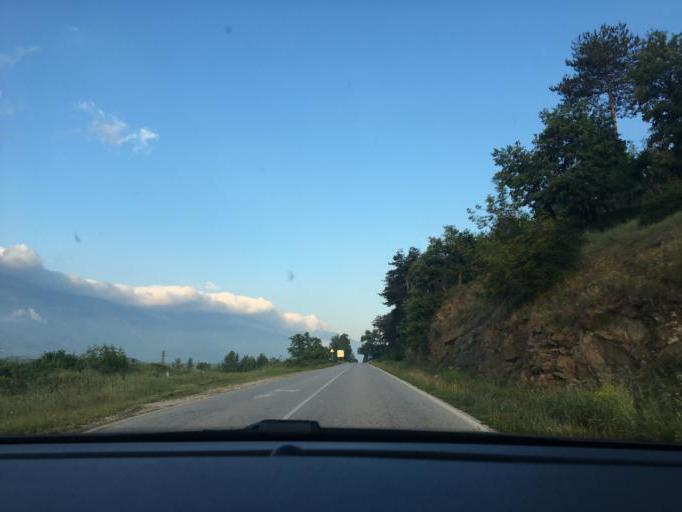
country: BG
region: Blagoevgrad
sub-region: Obshtina Petrich
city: Petrich
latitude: 41.3965
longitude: 23.0527
